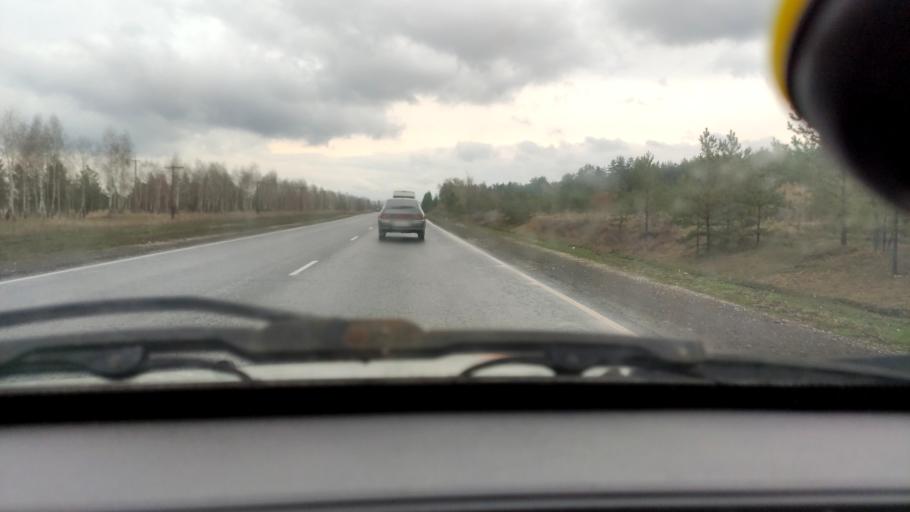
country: RU
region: Samara
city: Povolzhskiy
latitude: 53.5953
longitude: 49.5861
